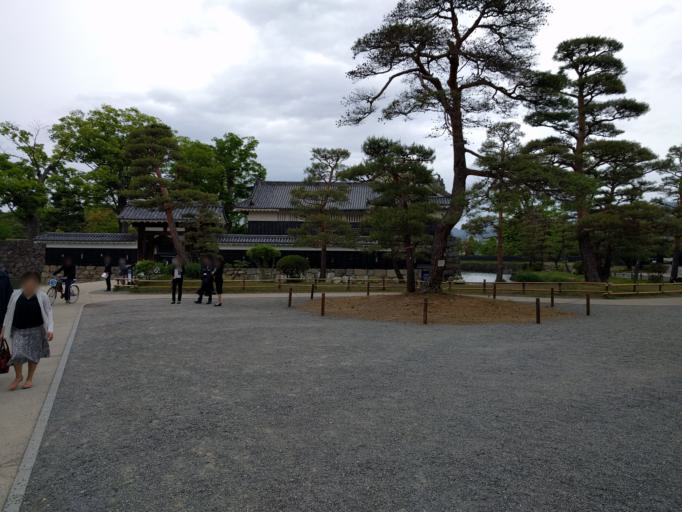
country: JP
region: Nagano
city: Matsumoto
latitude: 36.2376
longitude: 137.9700
